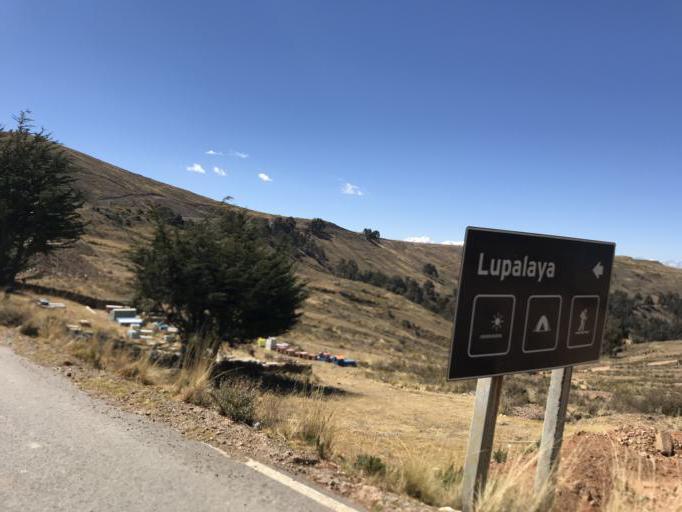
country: BO
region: La Paz
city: San Pablo
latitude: -16.2032
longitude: -68.8327
